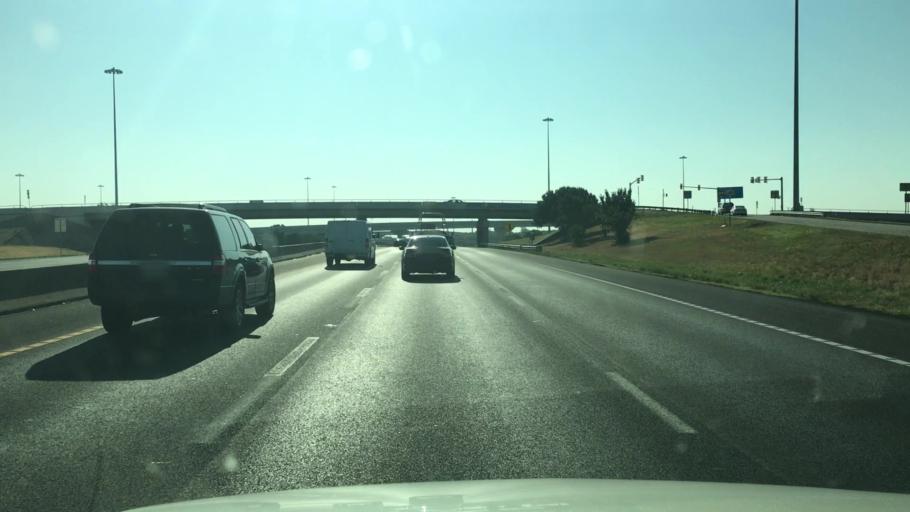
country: US
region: Texas
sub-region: Tarrant County
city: Richland Hills
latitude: 32.7597
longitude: -97.2193
